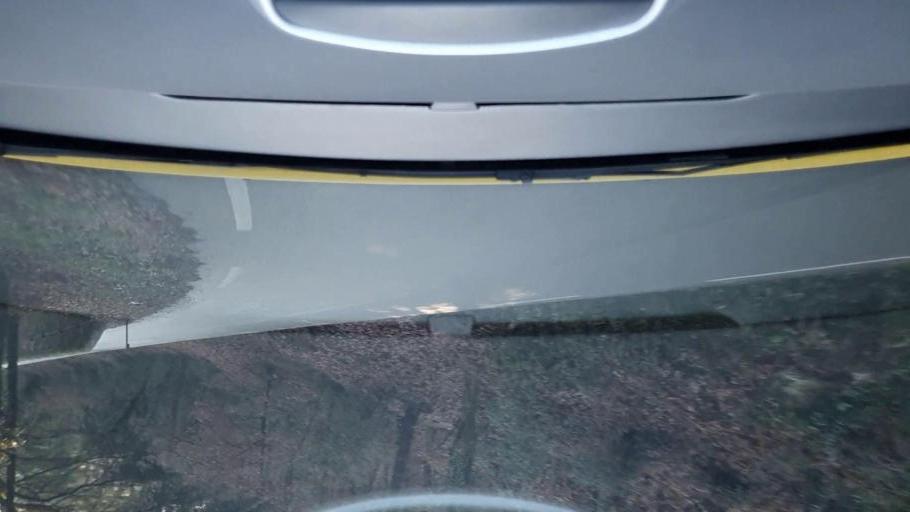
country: FR
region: Languedoc-Roussillon
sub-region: Departement du Gard
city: Branoux-les-Taillades
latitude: 44.3223
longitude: 3.9659
